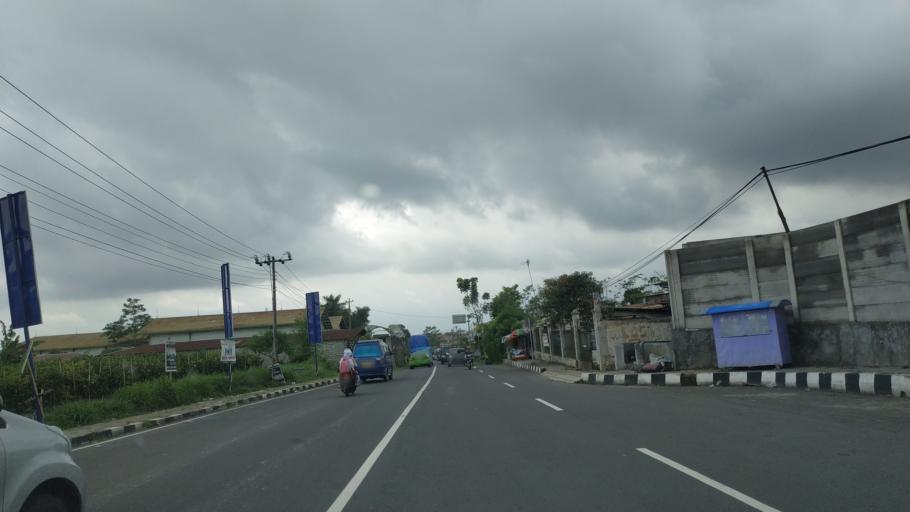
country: ID
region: Central Java
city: Magelang
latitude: -7.2847
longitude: 110.1105
